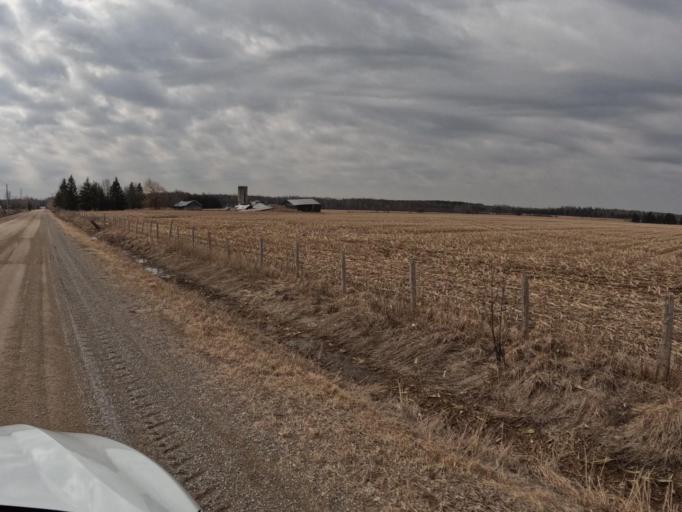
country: CA
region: Ontario
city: Orangeville
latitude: 43.9044
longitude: -80.2142
